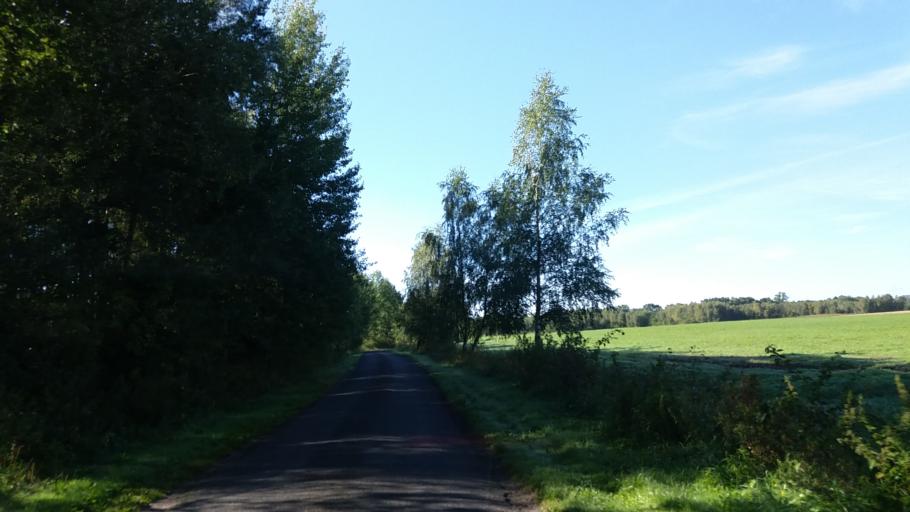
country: PL
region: West Pomeranian Voivodeship
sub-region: Powiat choszczenski
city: Choszczno
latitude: 53.1446
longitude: 15.4752
